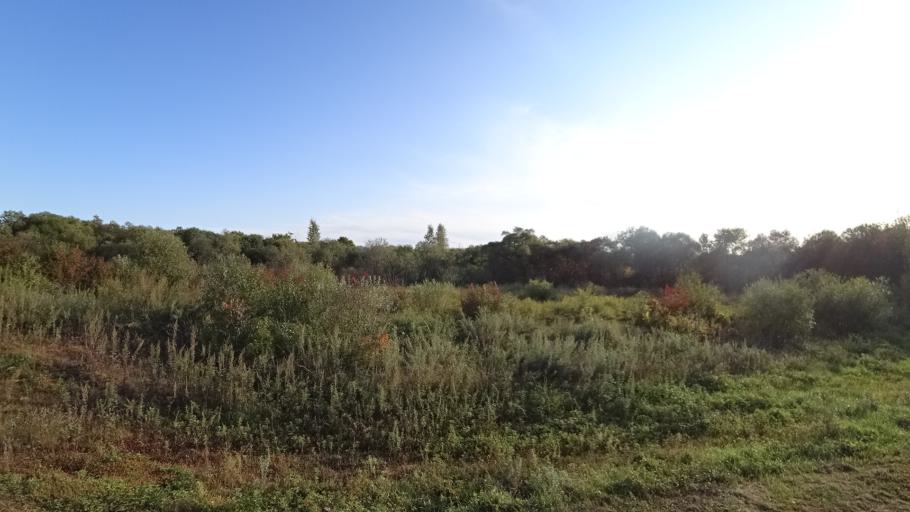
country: RU
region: Amur
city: Arkhara
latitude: 49.3597
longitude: 130.1266
